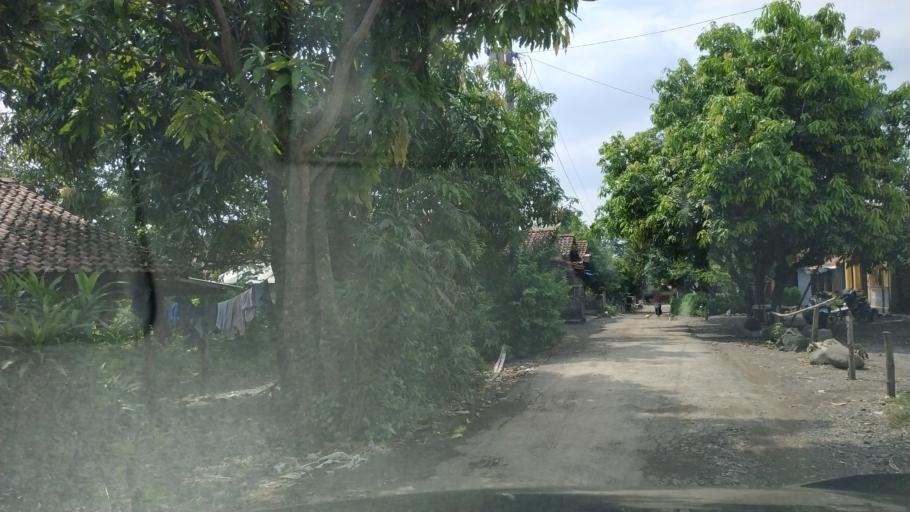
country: ID
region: Central Java
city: Margasari
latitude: -7.0950
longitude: 108.9734
